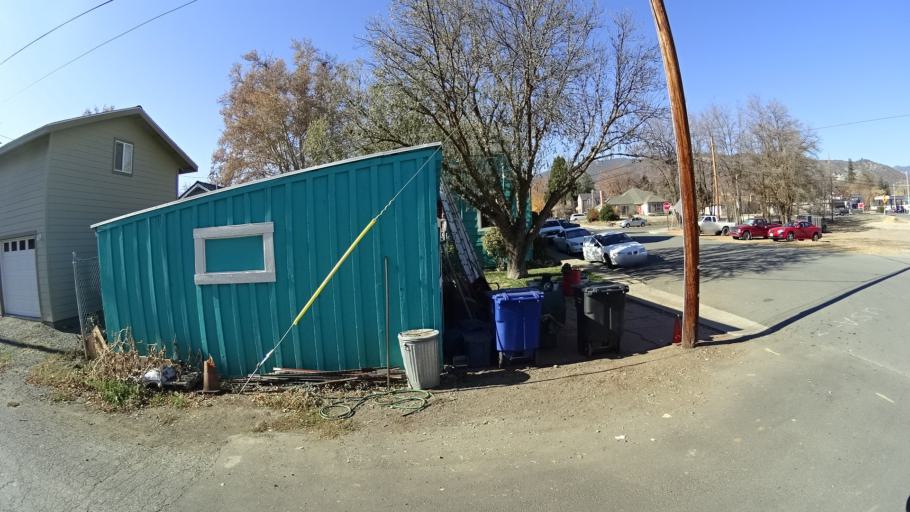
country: US
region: California
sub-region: Siskiyou County
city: Yreka
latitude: 41.7385
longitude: -122.6331
